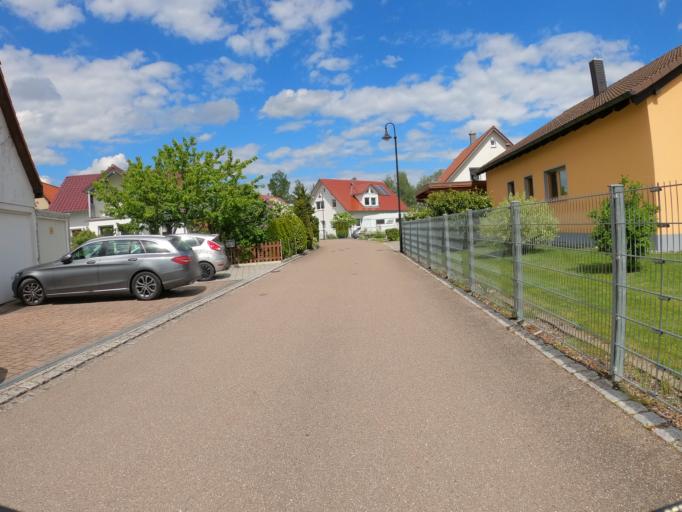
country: DE
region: Bavaria
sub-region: Swabia
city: Leipheim
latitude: 48.4579
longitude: 10.2160
